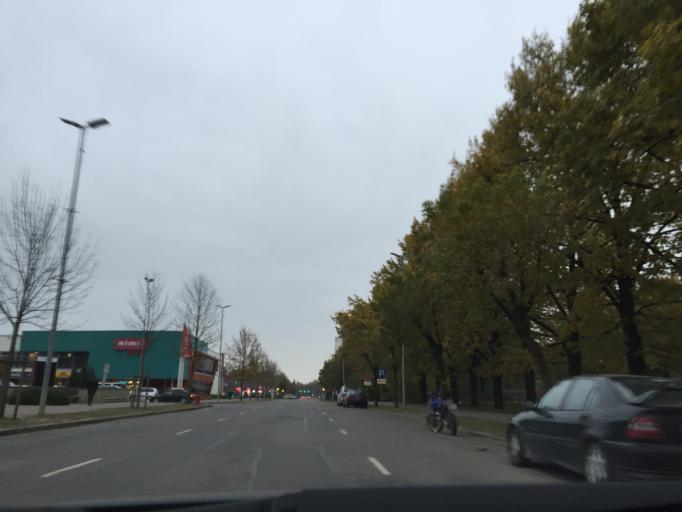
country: LV
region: Jelgava
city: Jelgava
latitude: 56.6485
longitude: 23.7246
